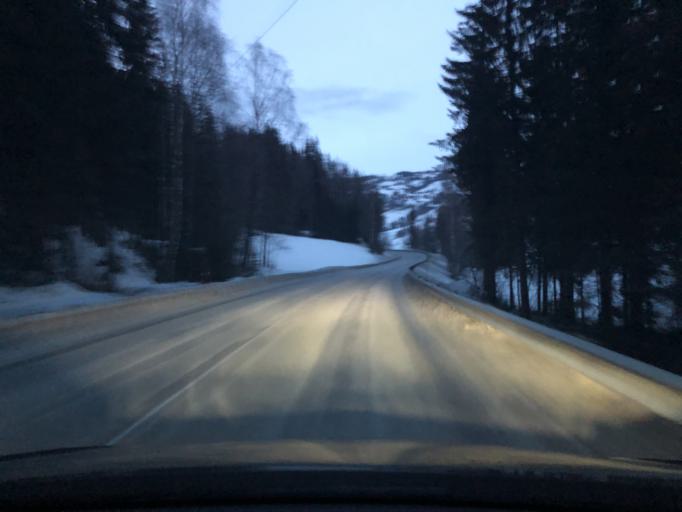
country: NO
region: Oppland
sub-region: Nord-Aurdal
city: Fagernes
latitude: 61.0031
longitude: 9.2094
